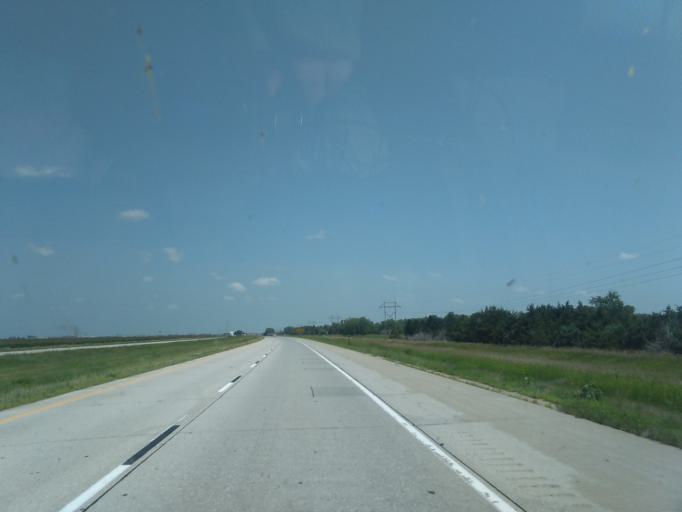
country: US
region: Nebraska
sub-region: Dawson County
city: Lexington
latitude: 40.7495
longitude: -99.7739
